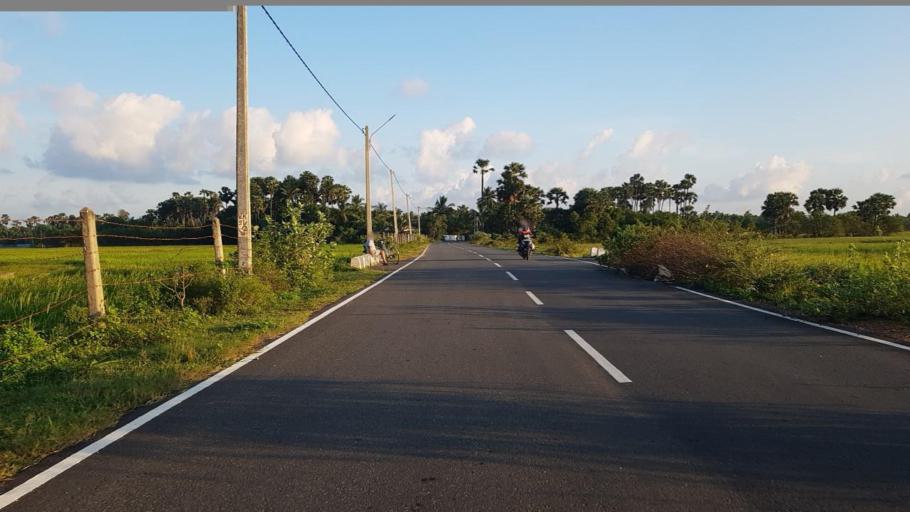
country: LK
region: Northern Province
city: Jaffna
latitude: 9.7245
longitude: 79.9766
